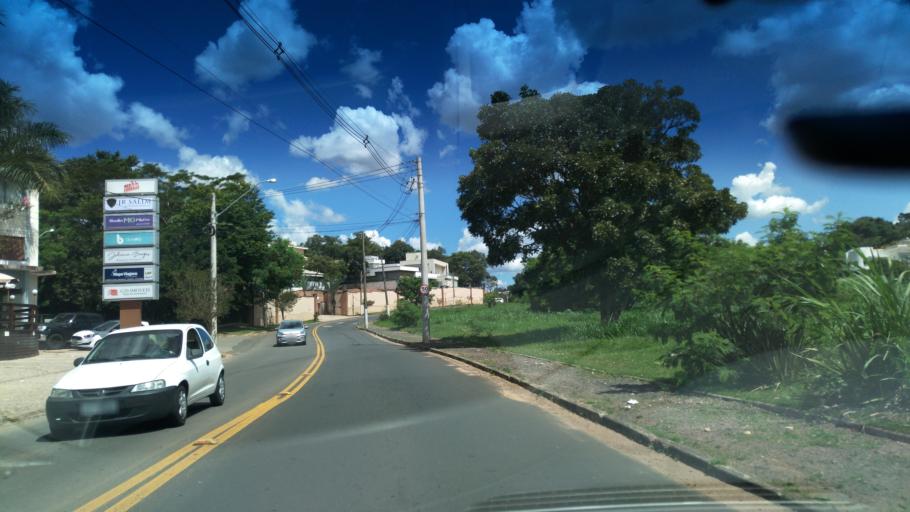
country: BR
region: Sao Paulo
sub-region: Valinhos
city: Valinhos
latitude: -22.9719
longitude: -47.0139
